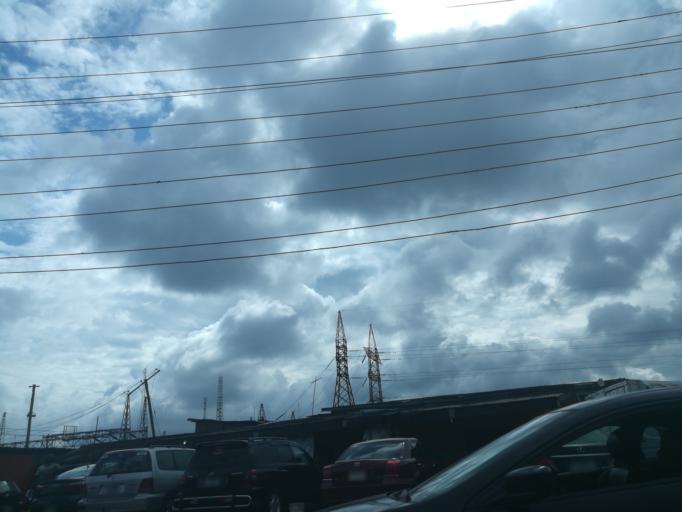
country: NG
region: Lagos
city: Agege
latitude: 6.6186
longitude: 3.3364
